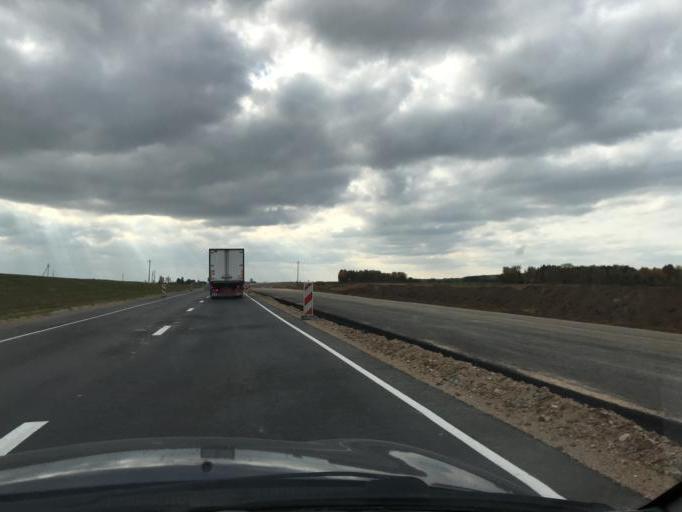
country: BY
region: Grodnenskaya
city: Lida
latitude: 53.8176
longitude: 25.1199
